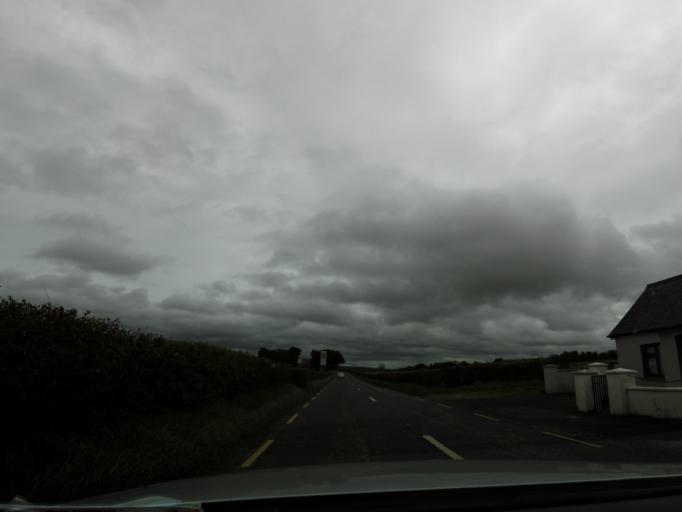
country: IE
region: Leinster
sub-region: Kilkenny
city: Ballyragget
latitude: 52.7231
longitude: -7.3532
